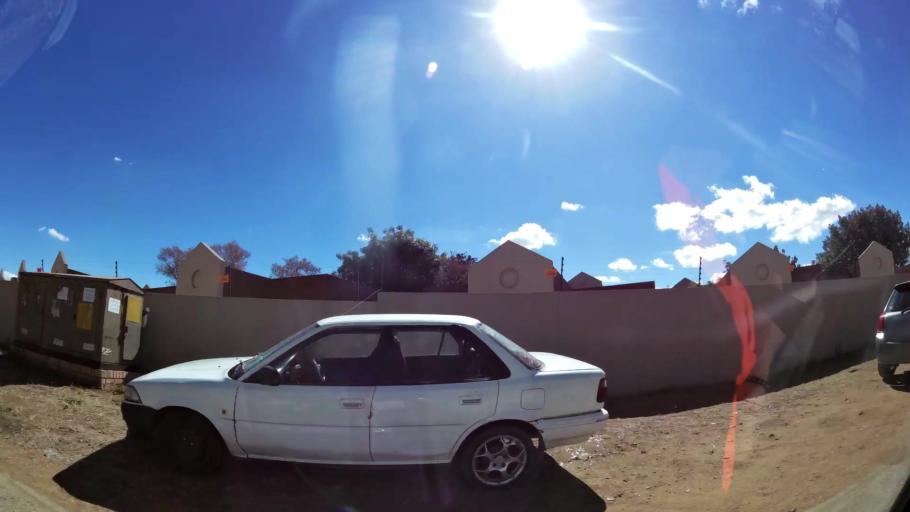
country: ZA
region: Limpopo
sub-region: Capricorn District Municipality
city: Polokwane
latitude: -23.9059
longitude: 29.4884
